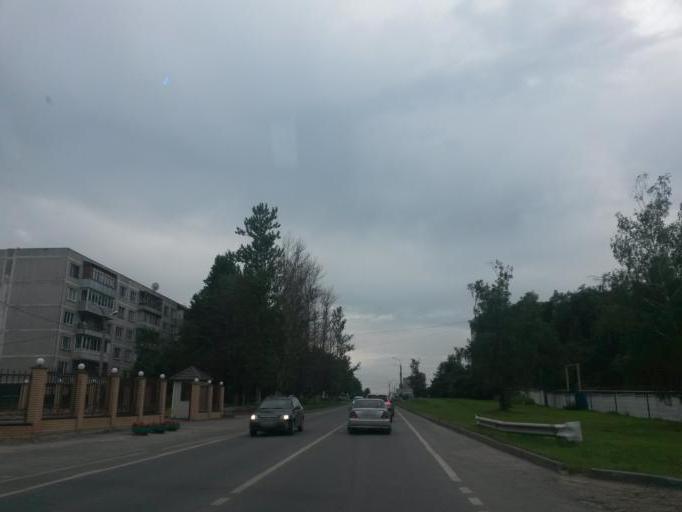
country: RU
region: Moskovskaya
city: Vostryakovo
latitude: 55.4184
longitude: 37.8390
